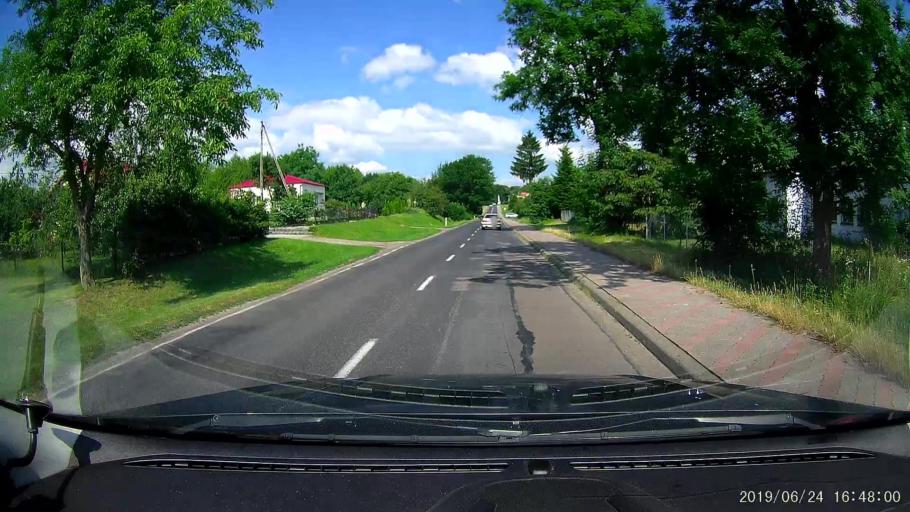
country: PL
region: Lublin Voivodeship
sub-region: Powiat tomaszowski
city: Laszczow
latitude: 50.5313
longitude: 23.7086
